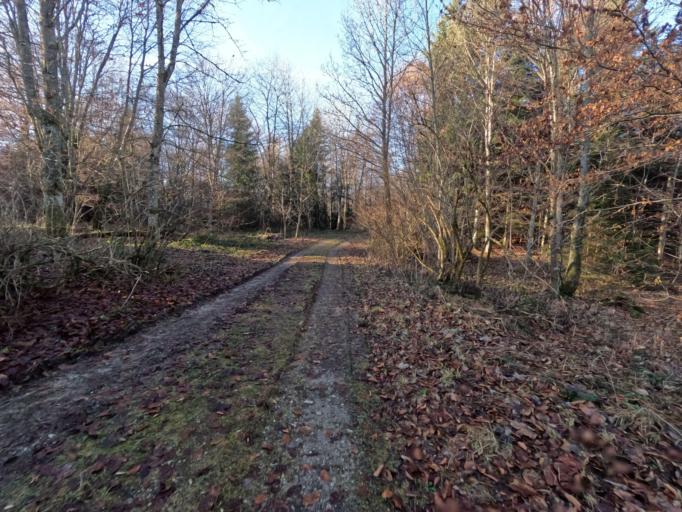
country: DE
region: Bavaria
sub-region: Upper Bavaria
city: Traunstein
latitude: 47.8954
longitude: 12.6277
